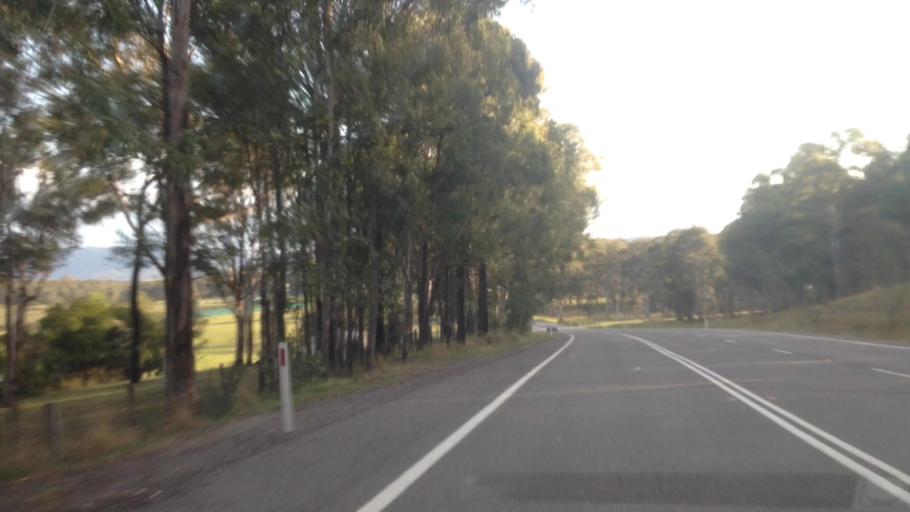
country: AU
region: New South Wales
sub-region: Cessnock
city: Kurri Kurri
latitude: -32.8616
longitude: 151.4828
